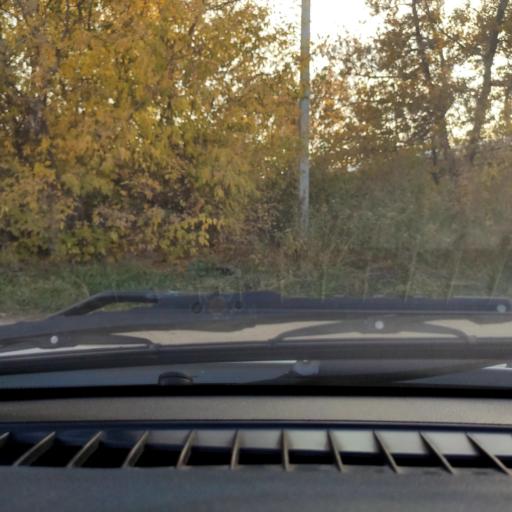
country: RU
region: Samara
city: Tol'yatti
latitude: 53.5275
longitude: 49.4605
